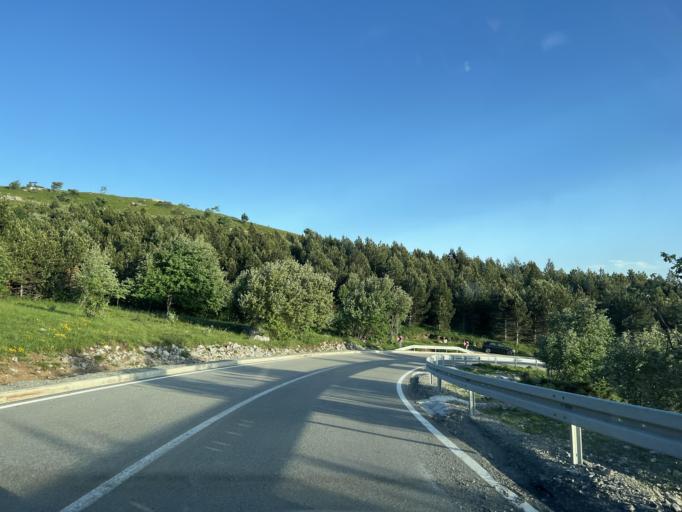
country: HR
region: Primorsko-Goranska
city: Podhum
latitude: 45.4067
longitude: 14.5538
